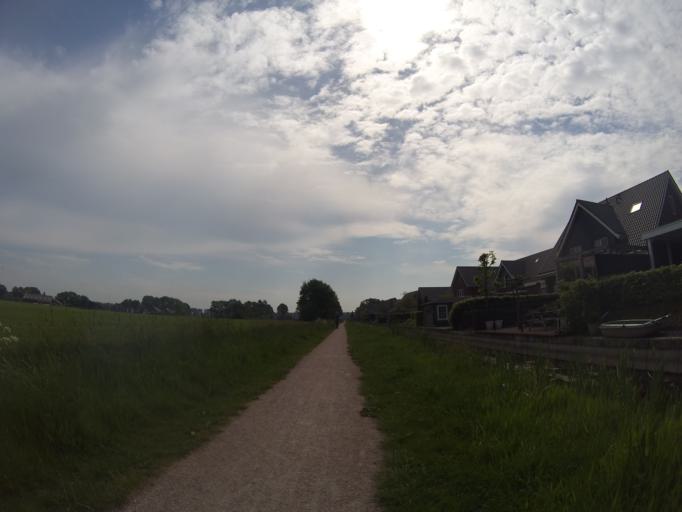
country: NL
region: Gelderland
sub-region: Gemeente Ede
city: Ederveen
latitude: 52.0781
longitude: 5.5488
